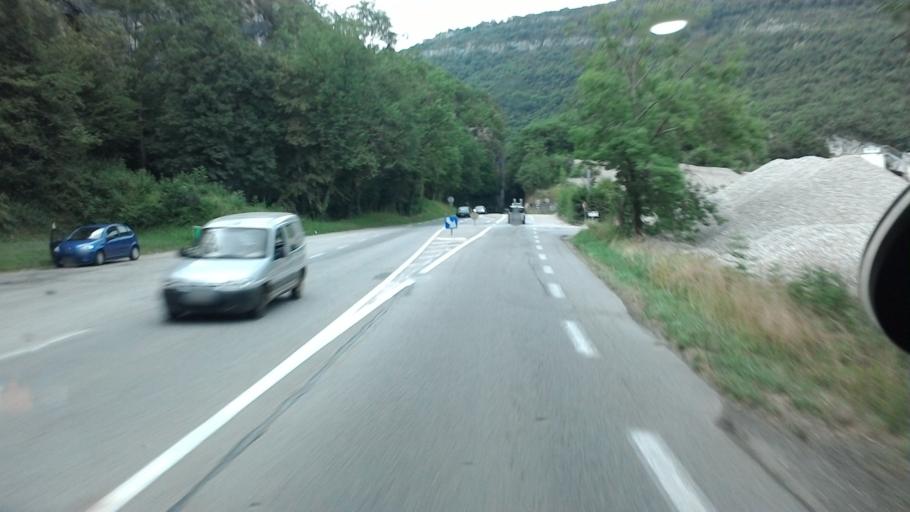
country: FR
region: Rhone-Alpes
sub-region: Departement de la Savoie
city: Yenne
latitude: 45.7068
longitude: 5.7365
